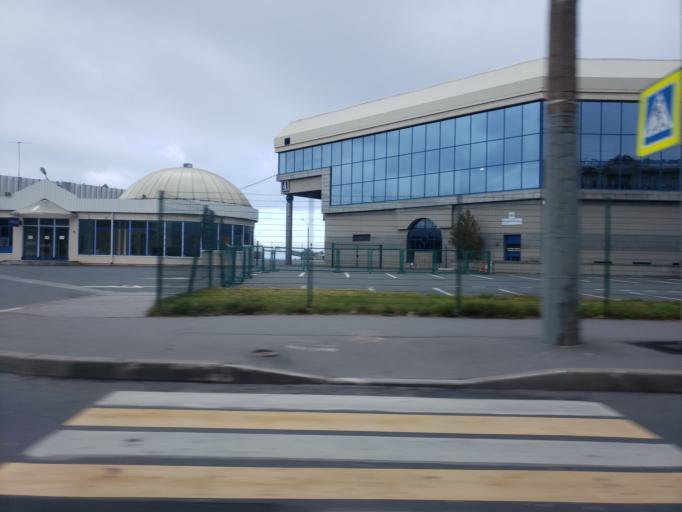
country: RU
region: St.-Petersburg
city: Vasyl'evsky Ostrov
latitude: 59.9297
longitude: 30.2370
